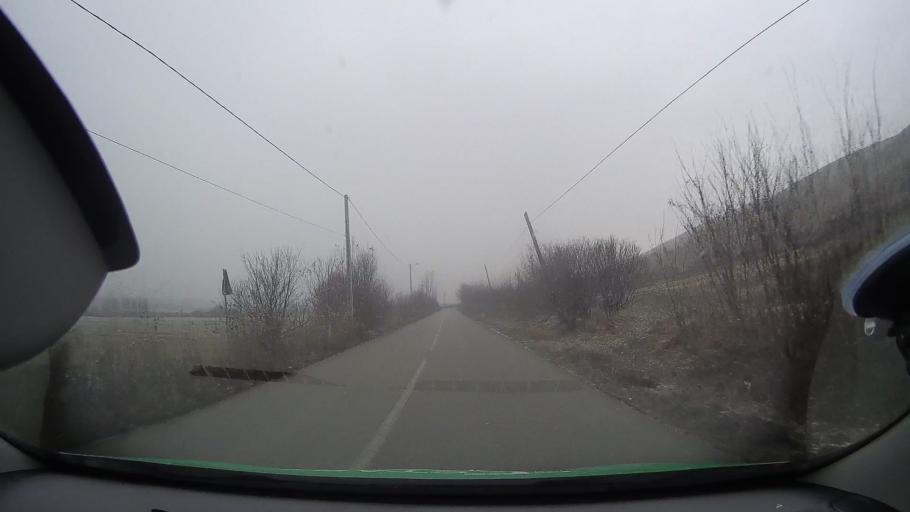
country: RO
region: Alba
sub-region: Comuna Farau
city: Farau
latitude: 46.3362
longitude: 23.9574
